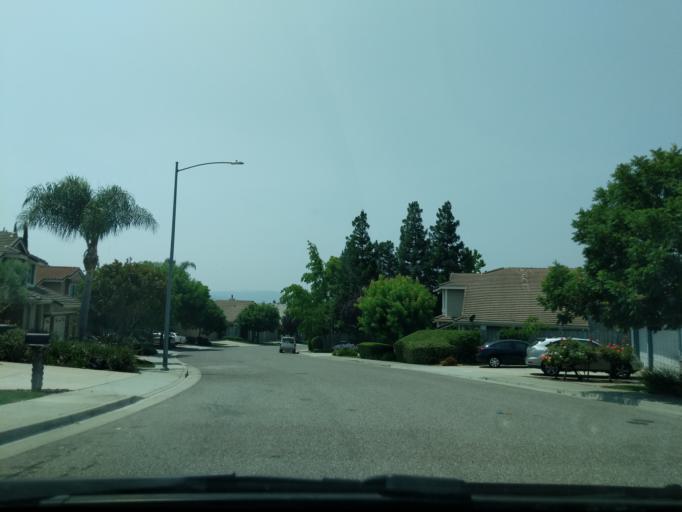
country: US
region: California
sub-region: Santa Clara County
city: San Martin
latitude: 37.1343
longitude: -121.6011
